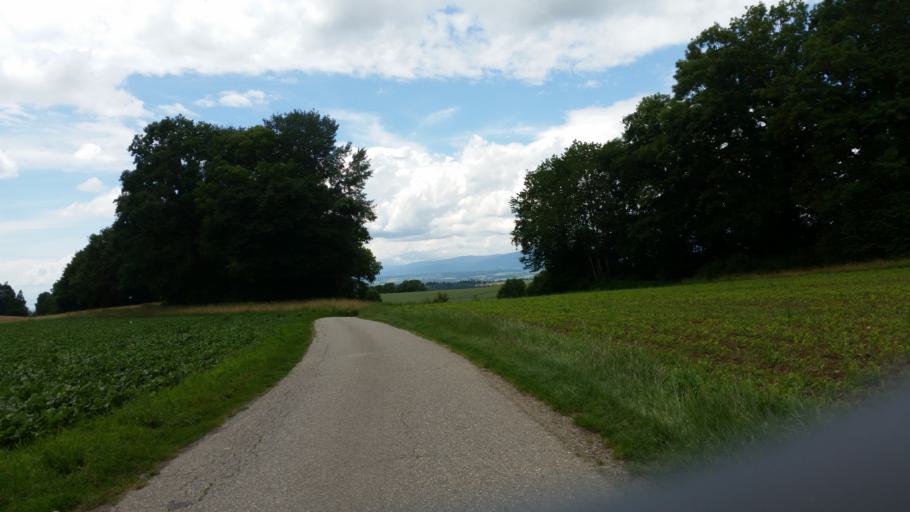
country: CH
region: Vaud
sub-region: Lausanne District
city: Cheseaux
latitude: 46.5987
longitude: 6.6219
